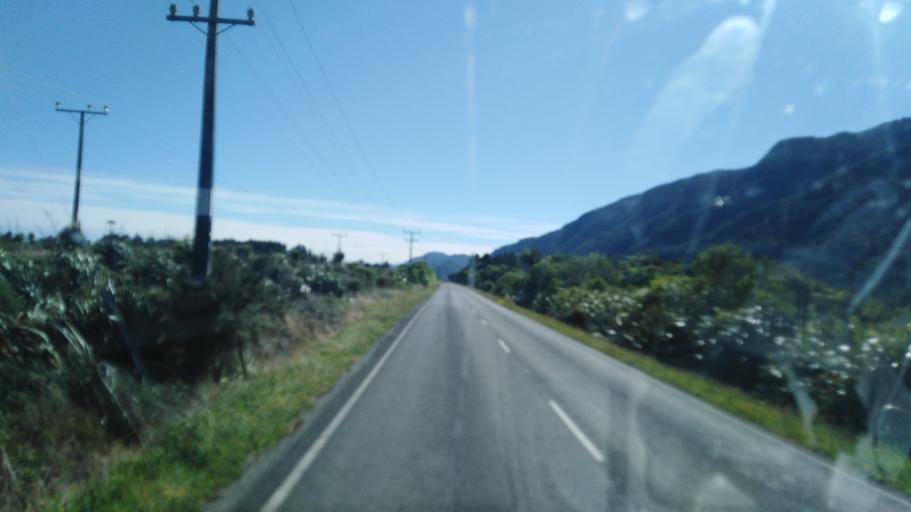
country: NZ
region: West Coast
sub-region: Buller District
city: Westport
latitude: -41.6600
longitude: 171.8183
